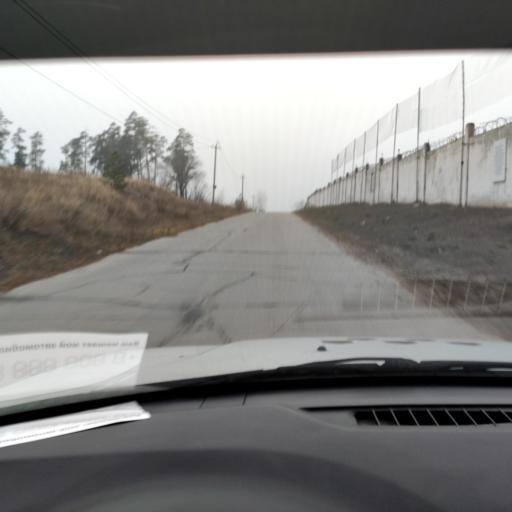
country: RU
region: Samara
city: Zhigulevsk
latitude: 53.4685
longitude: 49.5564
